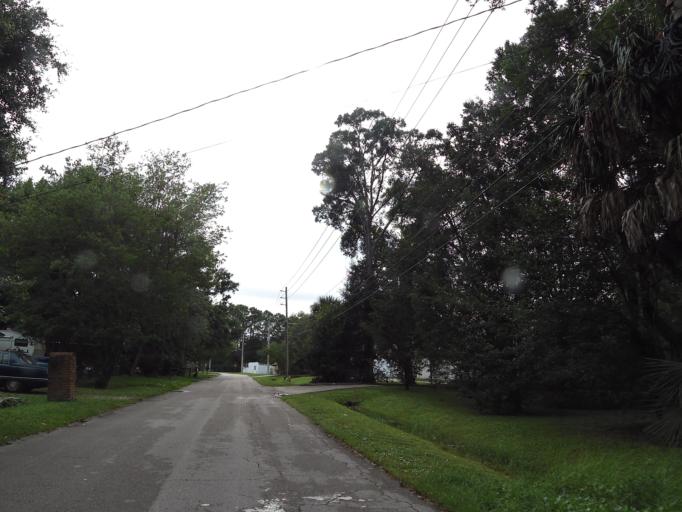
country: US
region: Florida
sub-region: Duval County
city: Jacksonville
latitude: 30.2930
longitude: -81.6246
